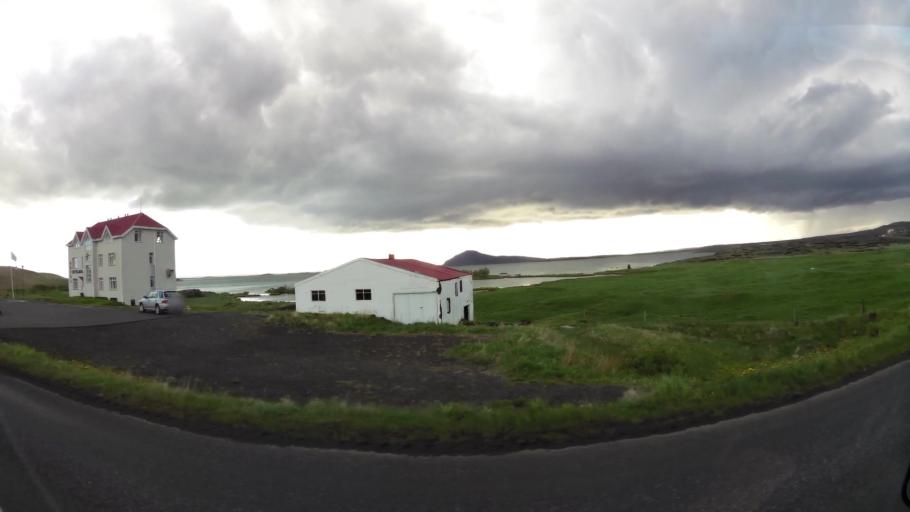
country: IS
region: Northeast
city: Laugar
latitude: 65.6429
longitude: -16.9127
